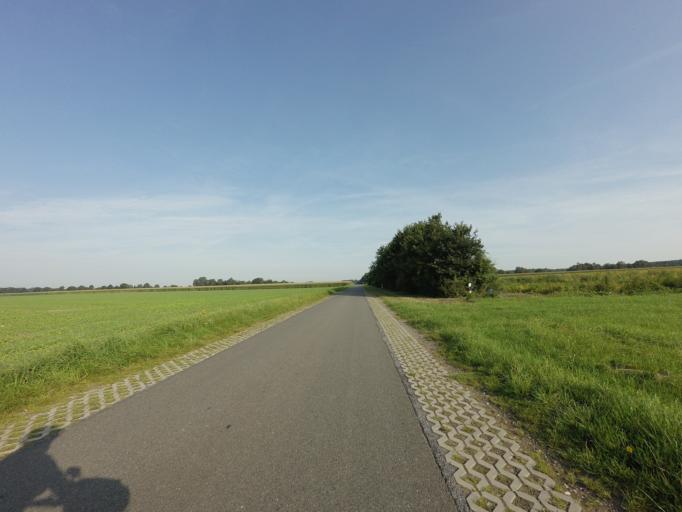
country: DE
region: Lower Saxony
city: Itterbeck
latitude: 52.4785
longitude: 6.8214
